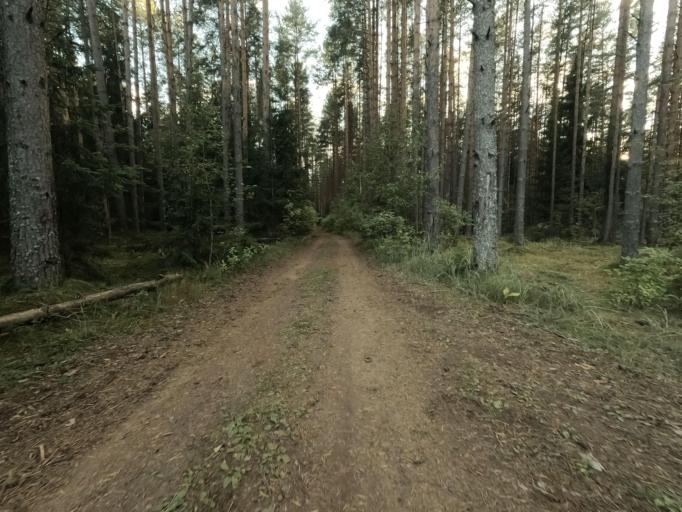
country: RU
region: Leningrad
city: Otradnoye
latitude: 59.8366
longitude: 30.7697
